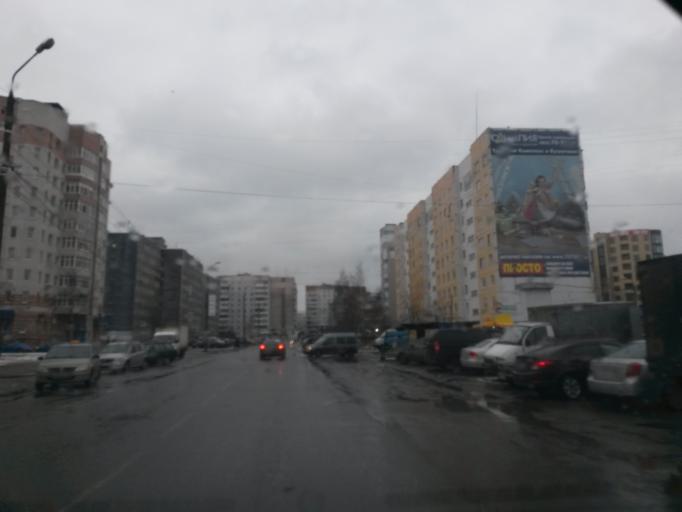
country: RU
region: Jaroslavl
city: Yaroslavl
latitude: 57.6506
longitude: 39.9498
